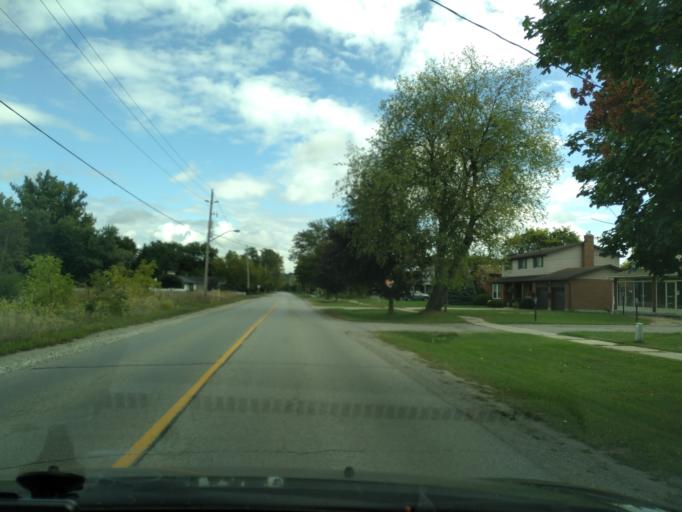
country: CA
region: Ontario
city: Newmarket
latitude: 44.1064
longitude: -79.5089
